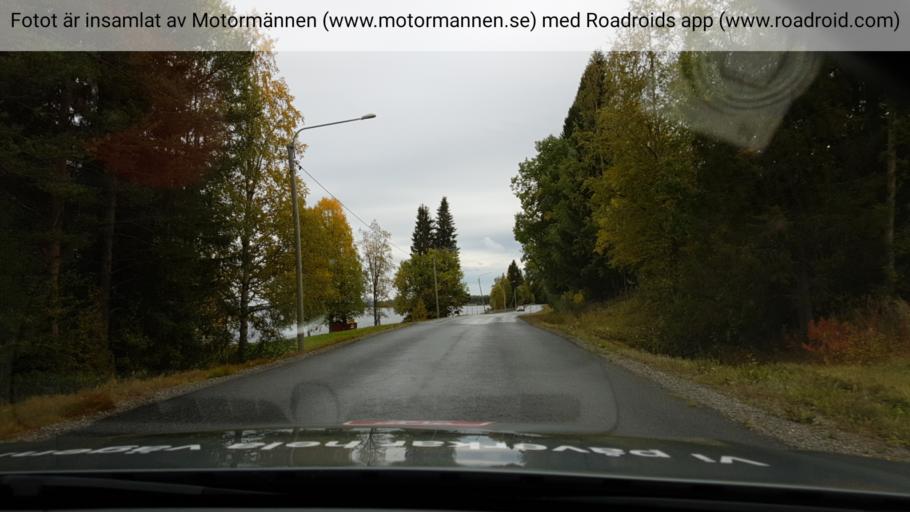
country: SE
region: Vaesterbotten
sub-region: Vilhelmina Kommun
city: Sjoberg
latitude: 64.6662
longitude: 16.3040
